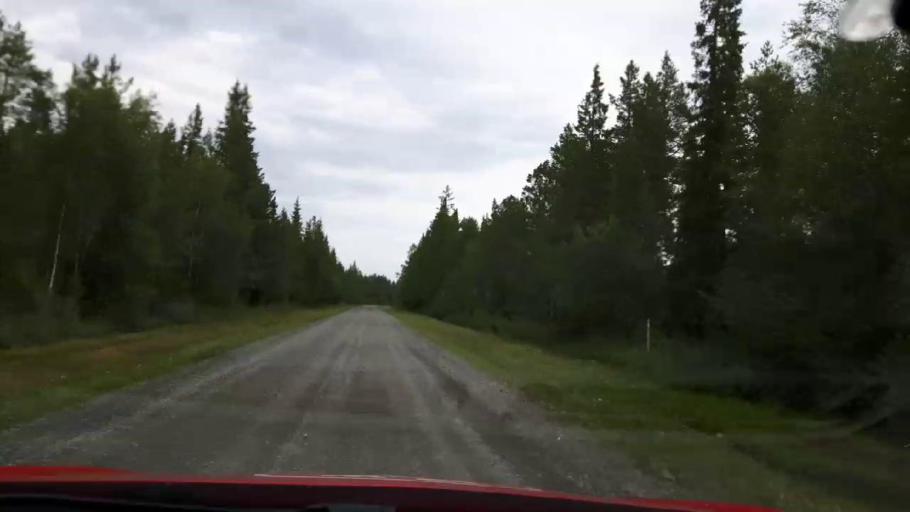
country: SE
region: Jaemtland
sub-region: Stroemsunds Kommun
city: Stroemsund
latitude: 63.7362
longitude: 15.5584
